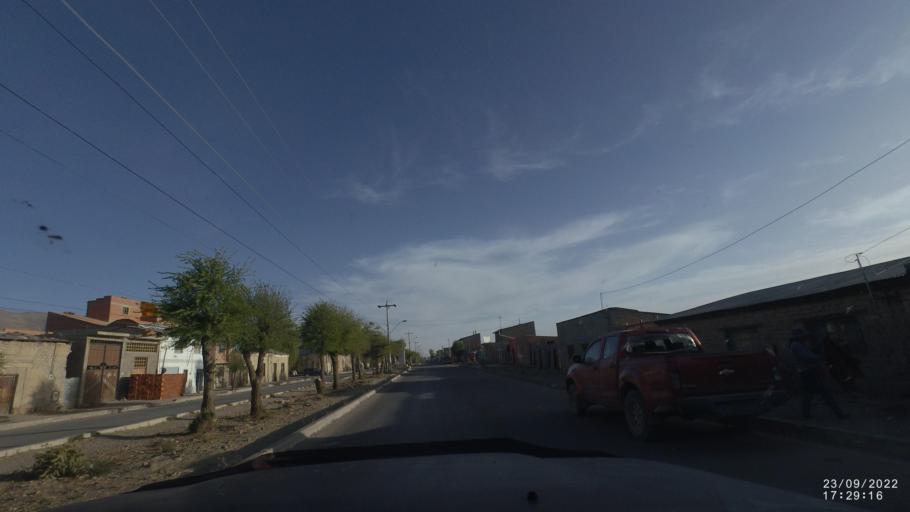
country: BO
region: Oruro
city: Challapata
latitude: -18.9015
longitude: -66.7769
